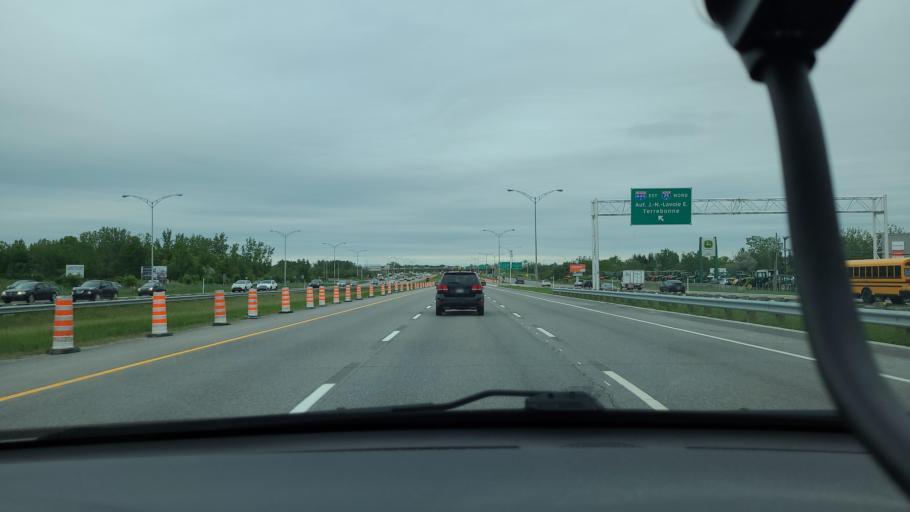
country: CA
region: Quebec
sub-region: Laval
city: Laval
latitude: 45.6142
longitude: -73.6766
